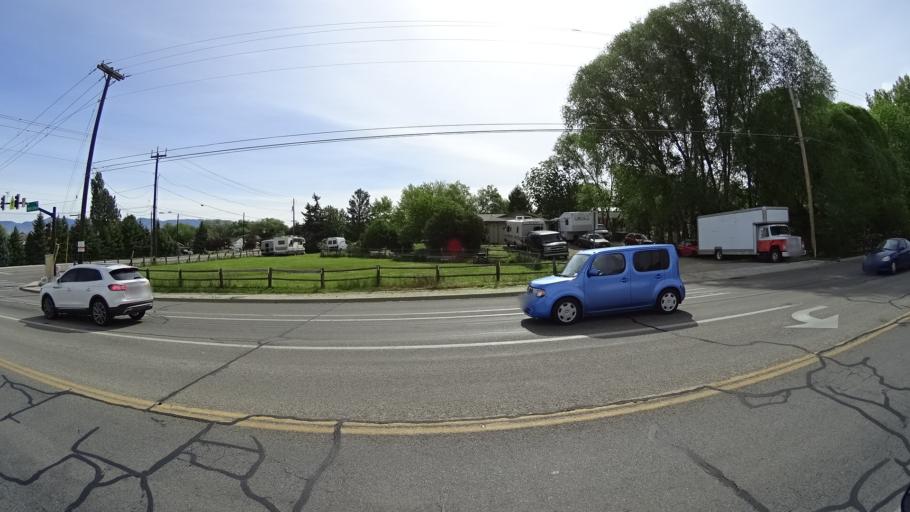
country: US
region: Idaho
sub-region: Ada County
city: Garden City
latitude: 43.5752
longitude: -116.2943
